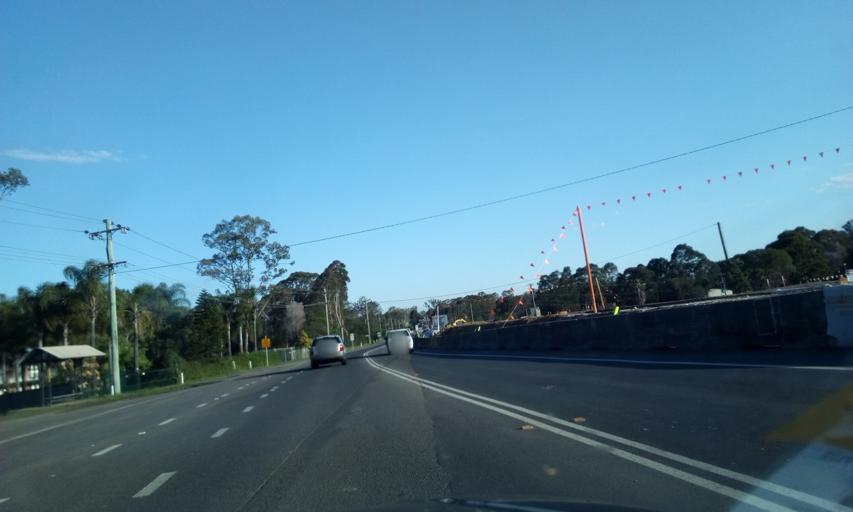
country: AU
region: New South Wales
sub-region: Liverpool
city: Bringelly
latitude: -33.9318
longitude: 150.7276
